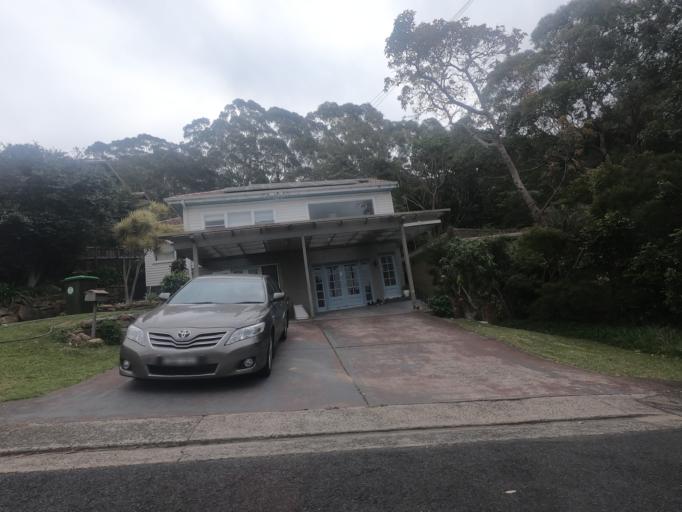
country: AU
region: New South Wales
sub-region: Wollongong
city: Bulli
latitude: -34.3043
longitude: 150.9298
